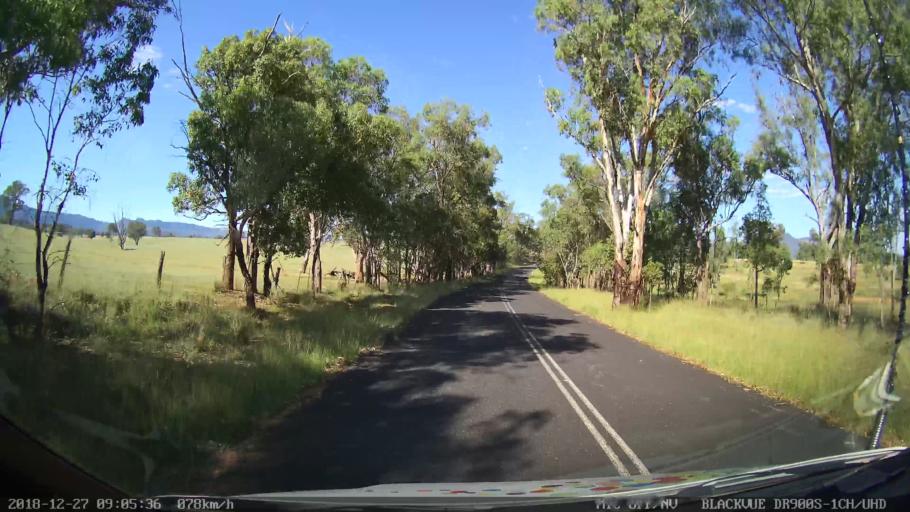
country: AU
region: New South Wales
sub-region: Lithgow
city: Portland
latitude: -33.1186
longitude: 150.1785
